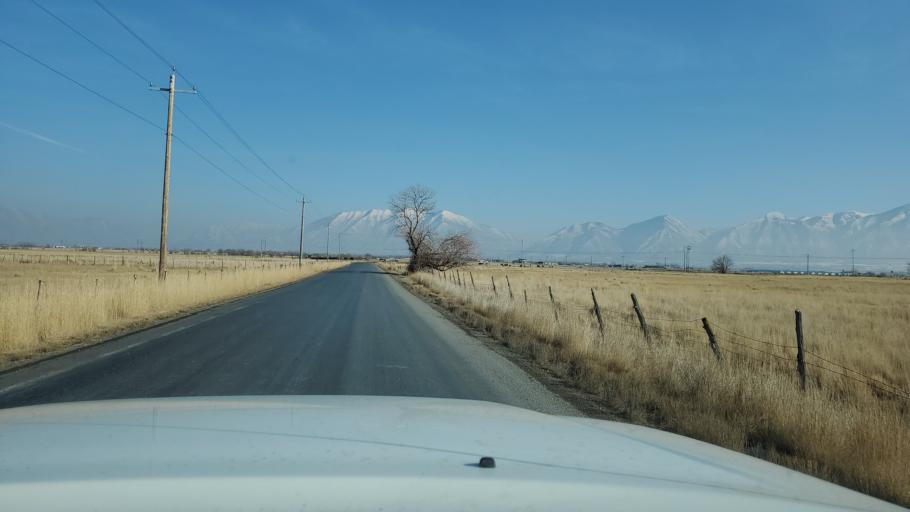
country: US
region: Utah
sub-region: Utah County
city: West Mountain
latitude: 40.0997
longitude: -111.7913
